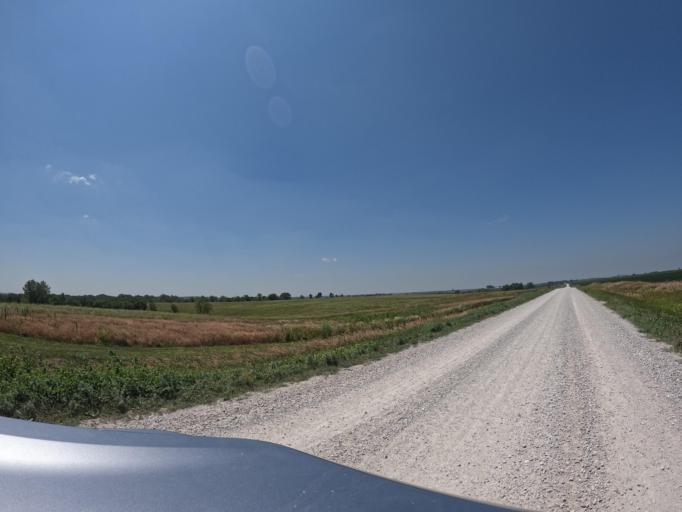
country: US
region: Iowa
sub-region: Keokuk County
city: Sigourney
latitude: 41.2578
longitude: -92.1824
